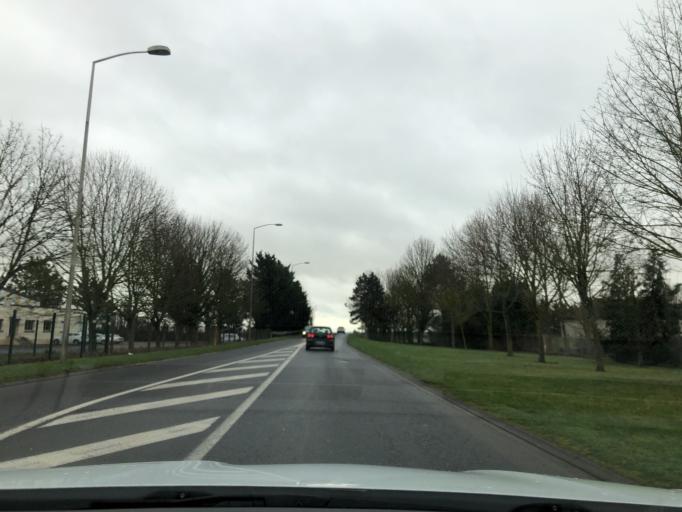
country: FR
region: Lower Normandy
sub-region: Departement du Calvados
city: Giberville
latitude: 49.1686
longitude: -0.2831
